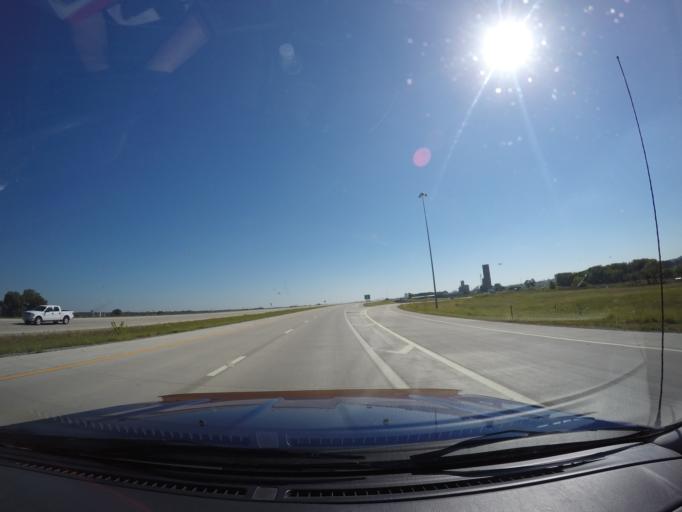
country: US
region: Kansas
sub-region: Shawnee County
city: Topeka
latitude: 39.0915
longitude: -95.7527
